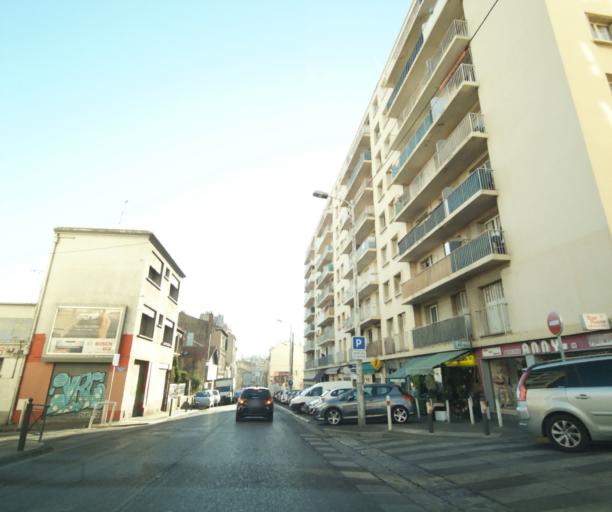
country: FR
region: Provence-Alpes-Cote d'Azur
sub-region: Departement des Bouches-du-Rhone
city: Marseille 13
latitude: 43.3208
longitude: 5.4100
